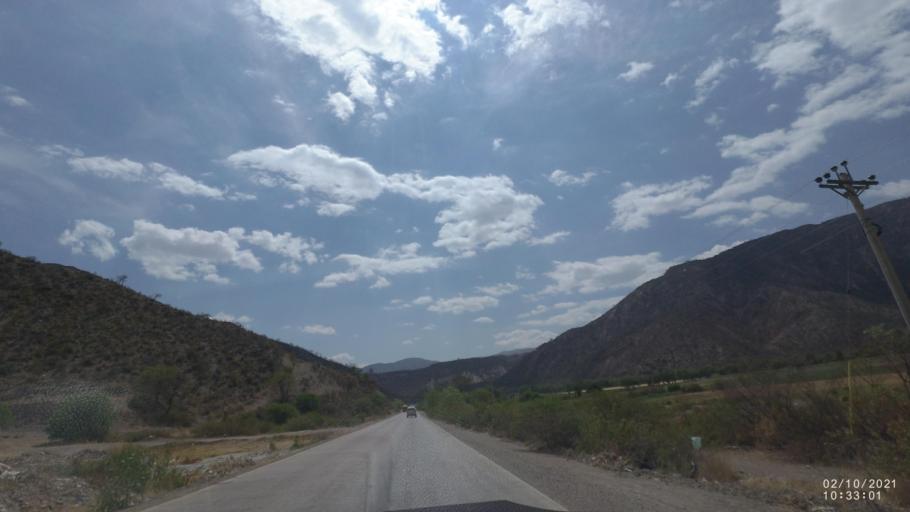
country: BO
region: Cochabamba
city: Capinota
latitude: -17.6834
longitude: -66.2584
